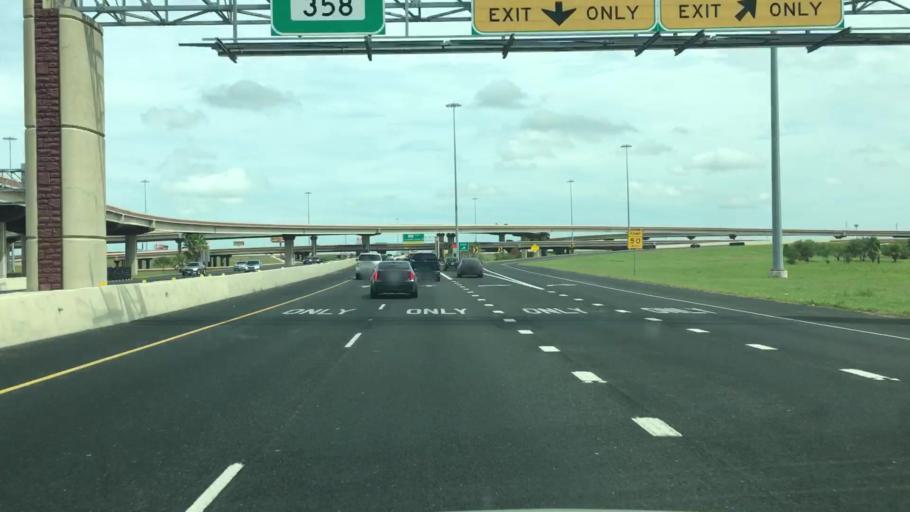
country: US
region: Texas
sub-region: Nueces County
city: Corpus Christi
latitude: 27.7389
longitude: -97.4343
